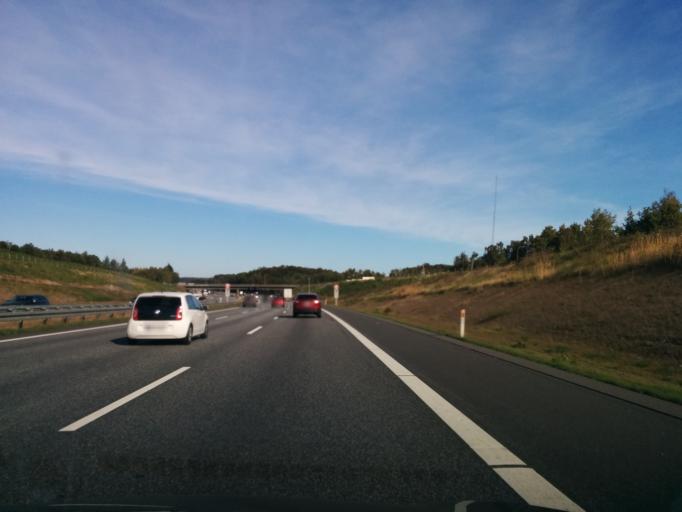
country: DK
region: South Denmark
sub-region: Vejle Kommune
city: Vejle
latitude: 55.6839
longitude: 9.5649
